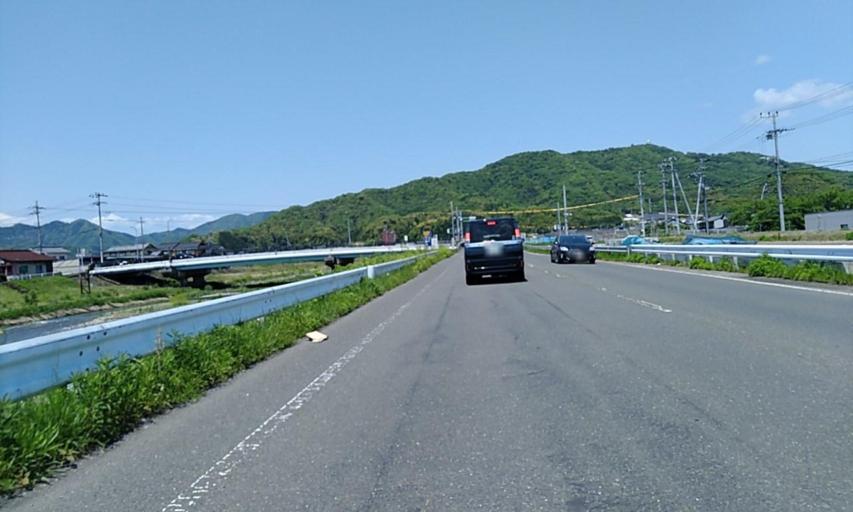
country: JP
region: Kyoto
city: Maizuru
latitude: 35.4439
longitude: 135.3364
